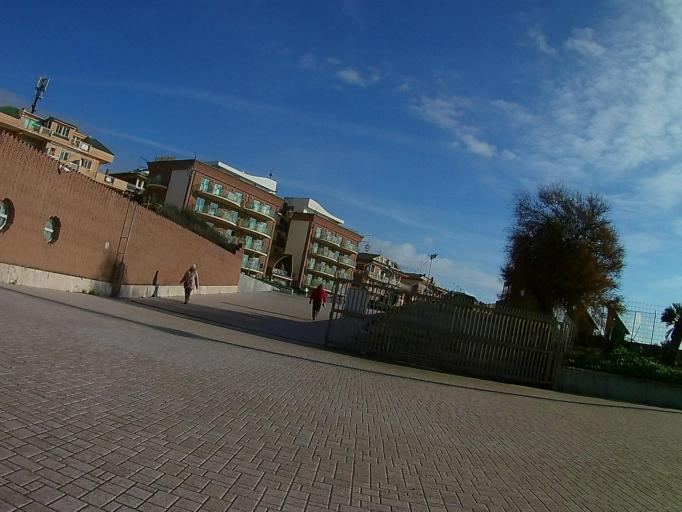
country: IT
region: Latium
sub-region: Citta metropolitana di Roma Capitale
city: Lido di Ostia
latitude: 41.7369
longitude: 12.2523
